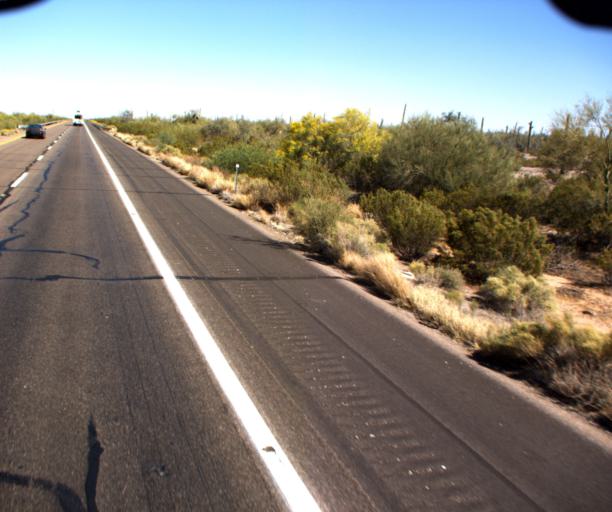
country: US
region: Arizona
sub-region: Pinal County
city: Maricopa
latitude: 32.8326
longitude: -112.0906
